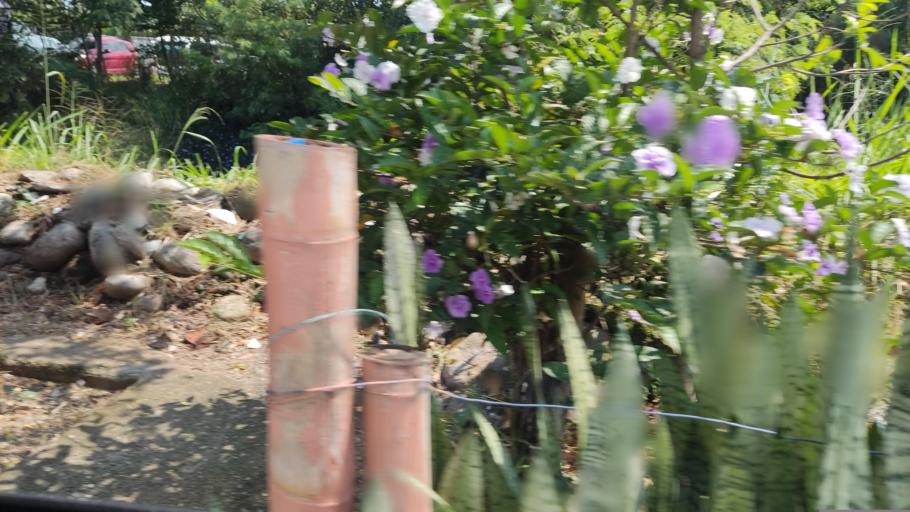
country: CO
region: Valle del Cauca
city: Cali
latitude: 3.4137
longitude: -76.5220
